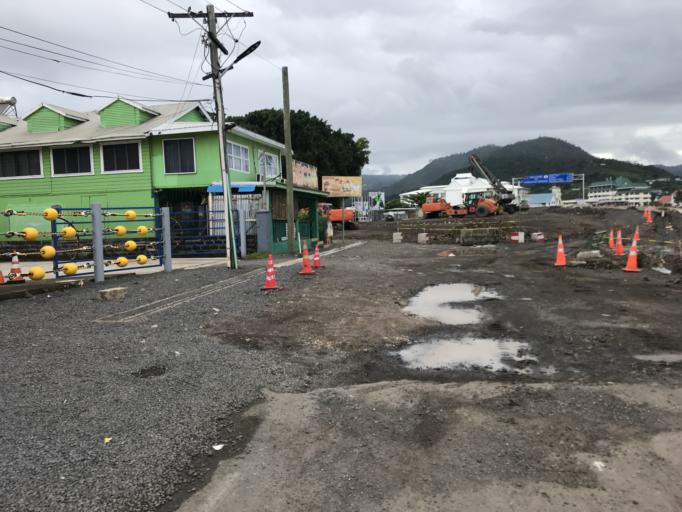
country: WS
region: Tuamasaga
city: Apia
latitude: -13.8301
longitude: -171.7596
